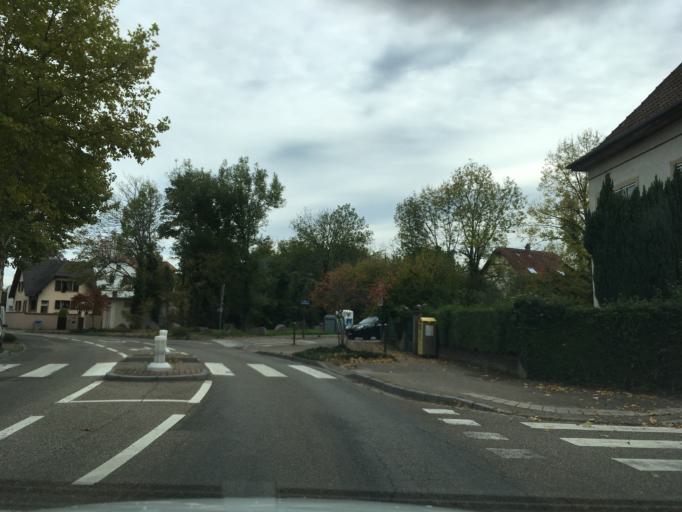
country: FR
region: Alsace
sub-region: Departement du Bas-Rhin
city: Hoenheim
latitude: 48.6193
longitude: 7.7937
